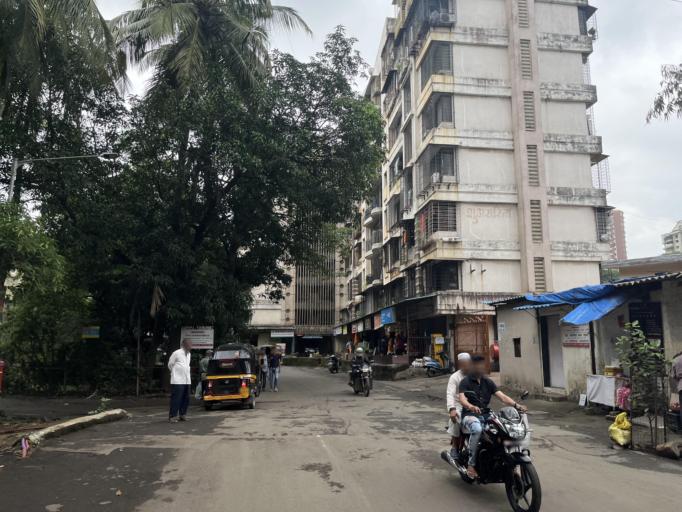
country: IN
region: Maharashtra
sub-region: Mumbai Suburban
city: Borivli
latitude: 19.2319
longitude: 72.8659
